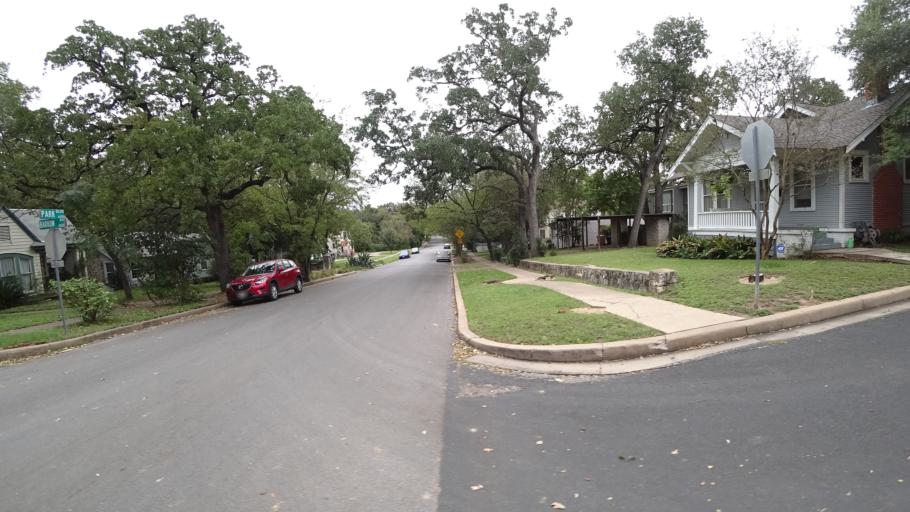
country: US
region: Texas
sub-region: Travis County
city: Austin
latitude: 30.3034
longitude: -97.7256
